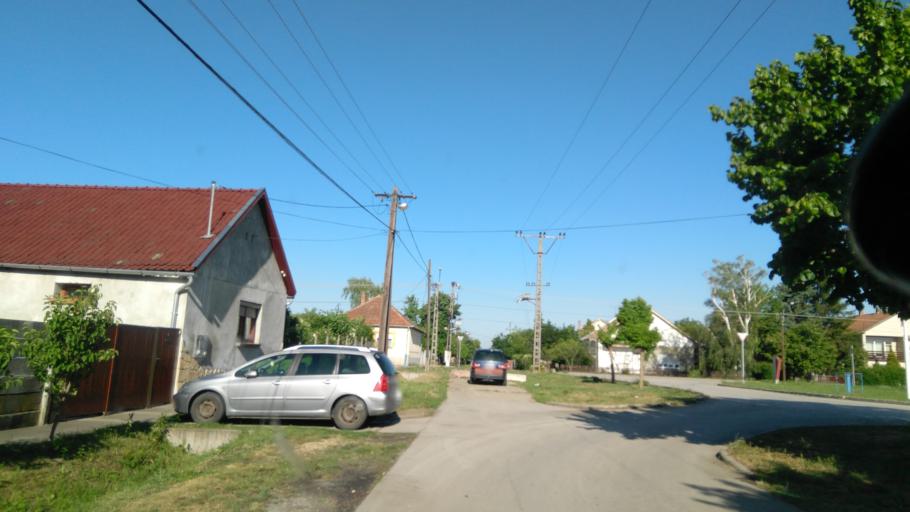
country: HU
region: Bekes
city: Elek
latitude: 46.5344
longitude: 21.2546
